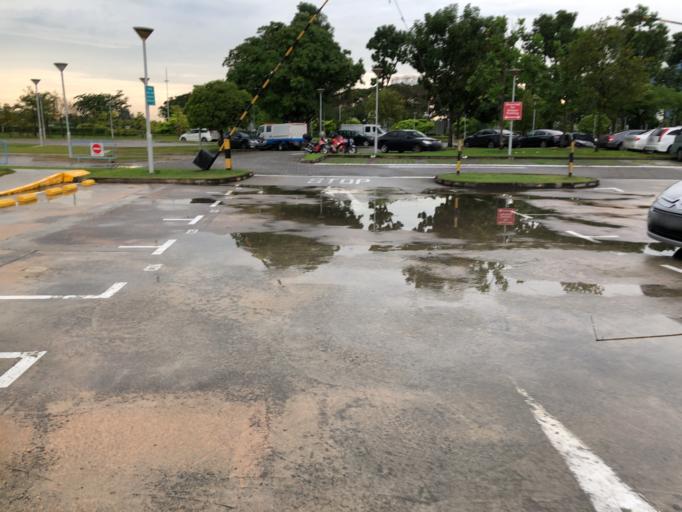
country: SG
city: Singapore
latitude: 1.2795
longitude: 103.8715
